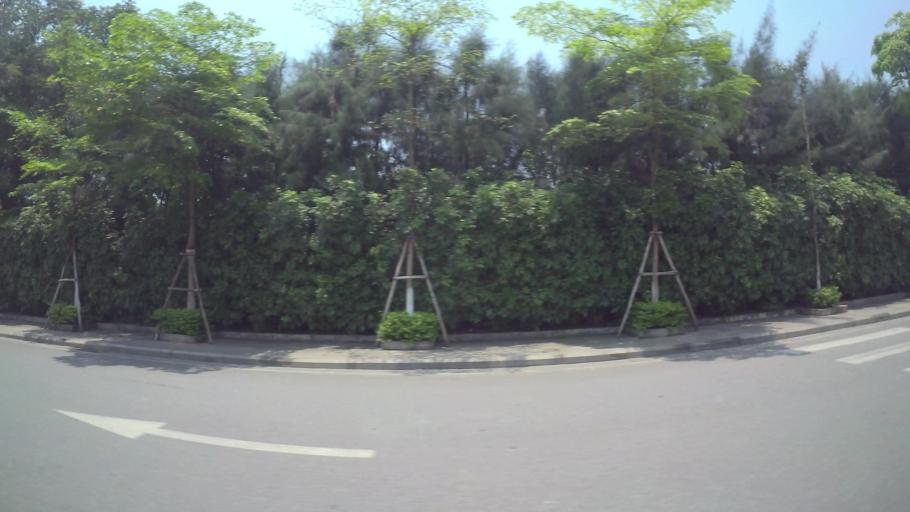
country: VN
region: Ha Noi
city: Trau Quy
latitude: 21.0356
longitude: 105.8962
